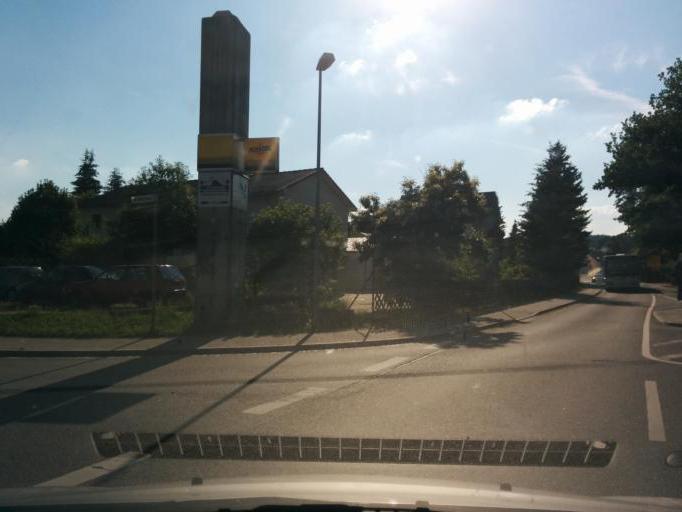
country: DE
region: Saxony
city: Floha
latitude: 50.8455
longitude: 13.0837
